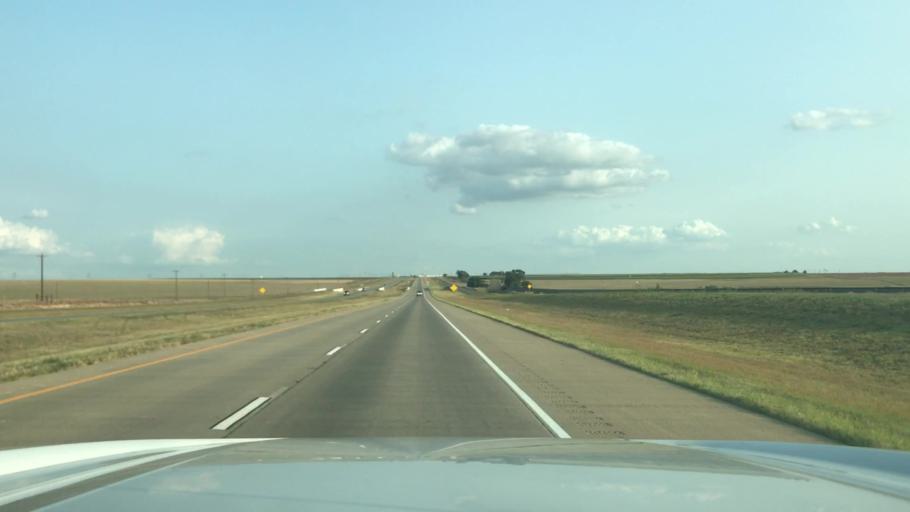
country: US
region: Texas
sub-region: Swisher County
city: Tulia
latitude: 34.6124
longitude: -101.8106
